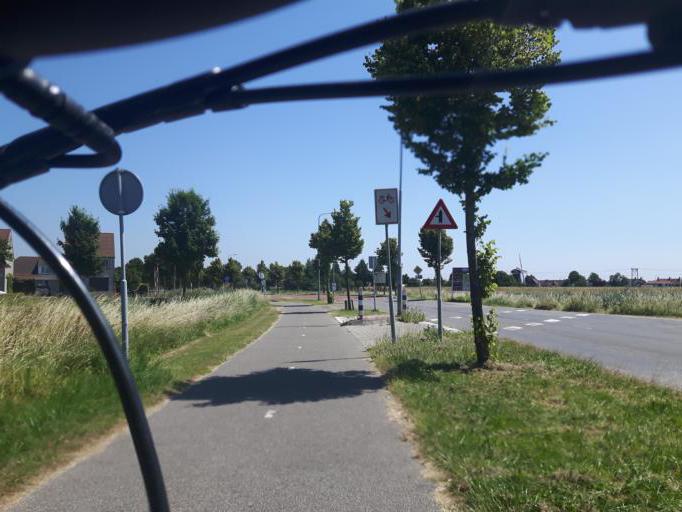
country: NL
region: Zeeland
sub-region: Gemeente Veere
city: Veere
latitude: 51.5035
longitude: 3.6652
